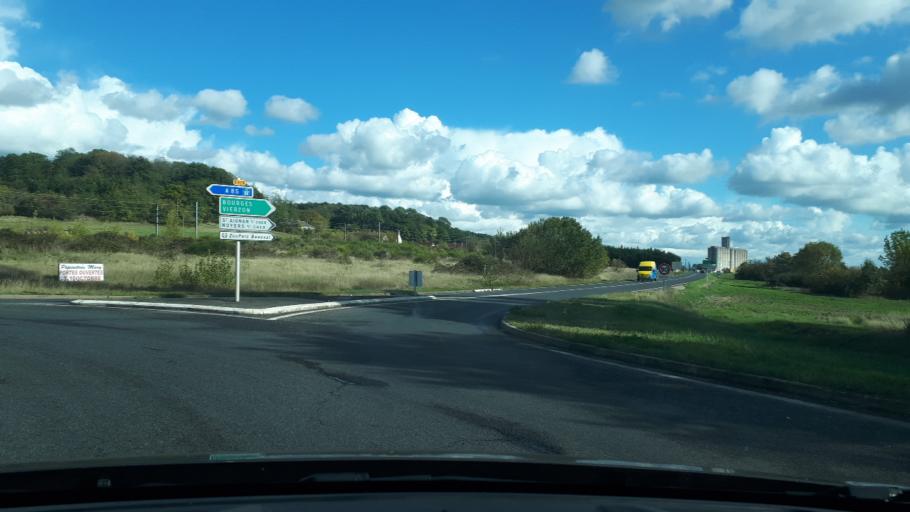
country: FR
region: Centre
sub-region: Departement du Loir-et-Cher
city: Mareuil-sur-Cher
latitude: 47.3022
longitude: 1.3499
